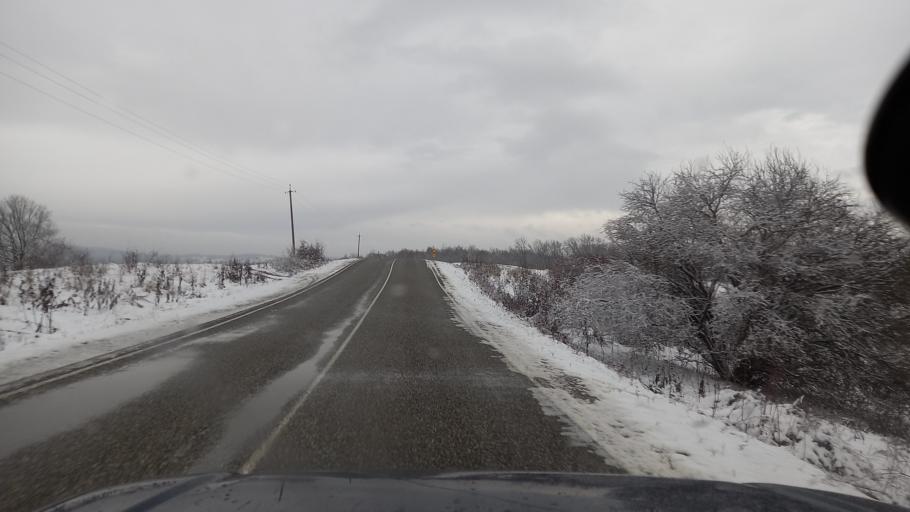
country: RU
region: Adygeya
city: Abadzekhskaya
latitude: 44.3450
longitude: 40.3590
